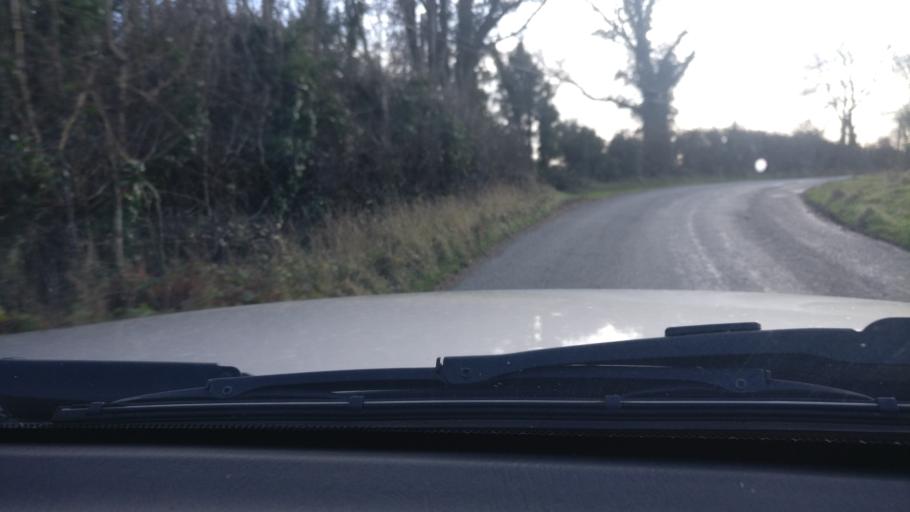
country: IE
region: Connaught
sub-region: County Galway
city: Ballinasloe
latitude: 53.2231
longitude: -8.2912
